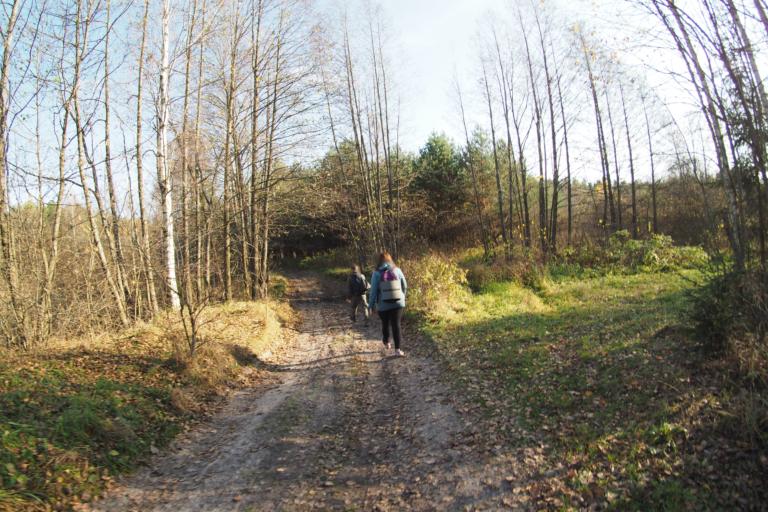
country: RU
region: Moskovskaya
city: Davydovo
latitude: 55.5454
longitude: 38.8192
